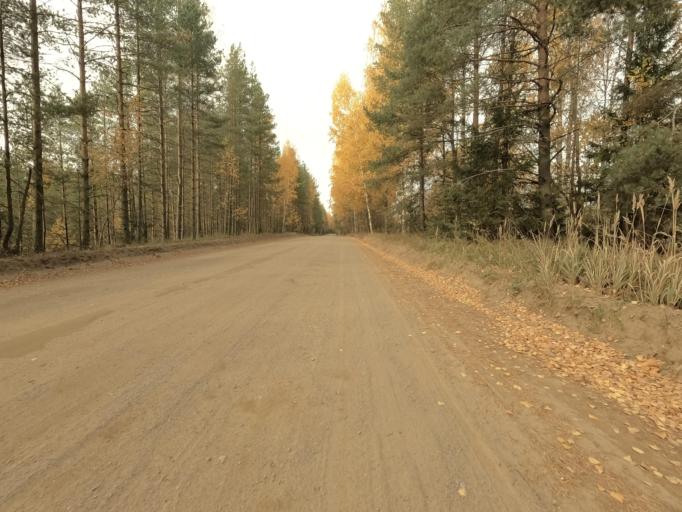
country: RU
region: Leningrad
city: Priladozhskiy
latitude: 59.6822
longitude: 31.3633
